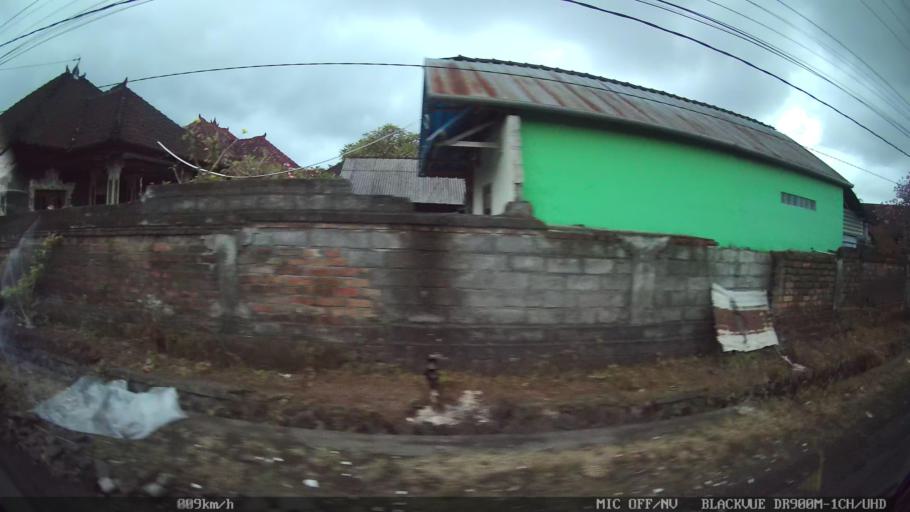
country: ID
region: Bali
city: Banjar Cemenggon
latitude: -8.5261
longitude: 115.1904
